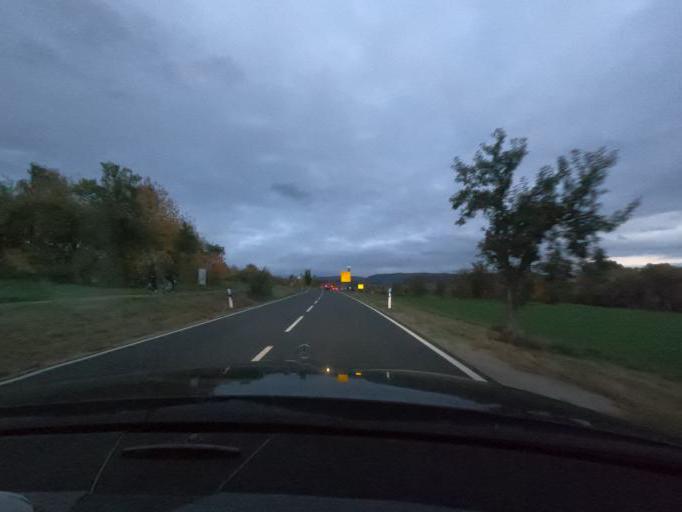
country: DE
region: Thuringia
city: Arenshausen
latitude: 51.3896
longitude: 9.9529
